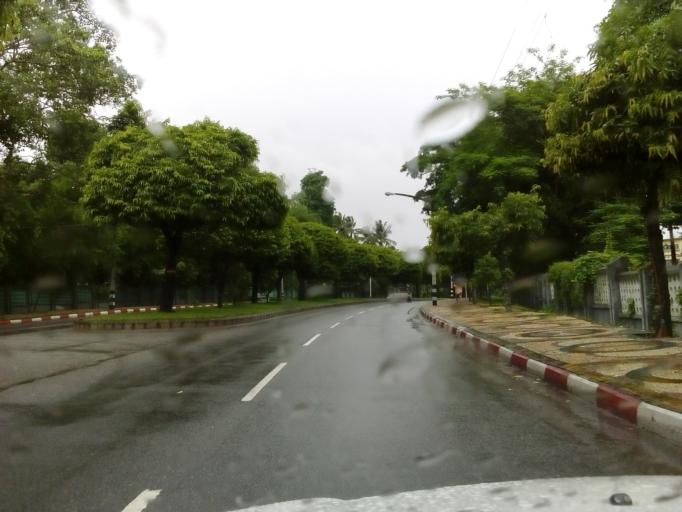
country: MM
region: Yangon
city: Yangon
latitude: 16.7930
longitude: 96.1480
